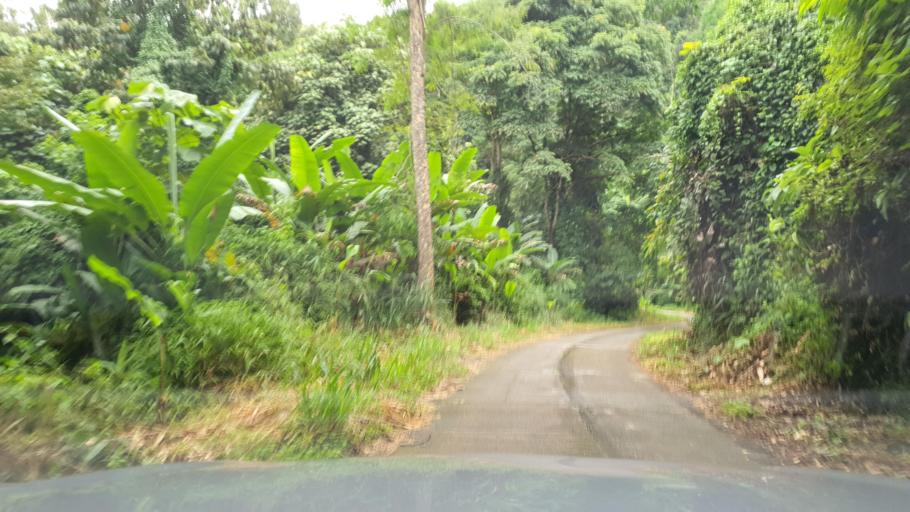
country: TH
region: Chiang Mai
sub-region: Amphoe Chiang Dao
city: Chiang Dao
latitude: 19.2712
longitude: 98.9373
